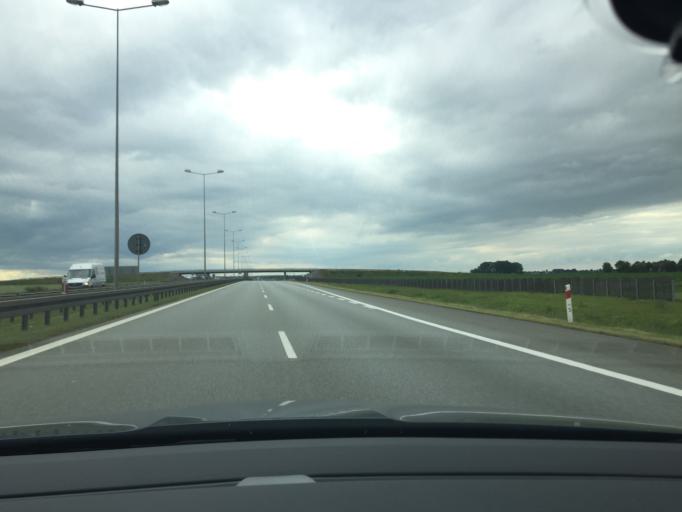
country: PL
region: Greater Poland Voivodeship
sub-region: Powiat poznanski
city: Dopiewo
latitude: 52.3502
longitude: 16.7224
